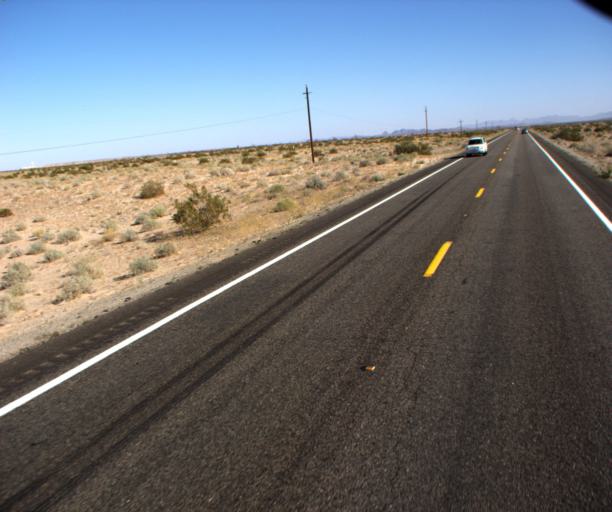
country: US
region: Arizona
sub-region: Yuma County
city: Fortuna Foothills
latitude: 32.8410
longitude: -114.3686
